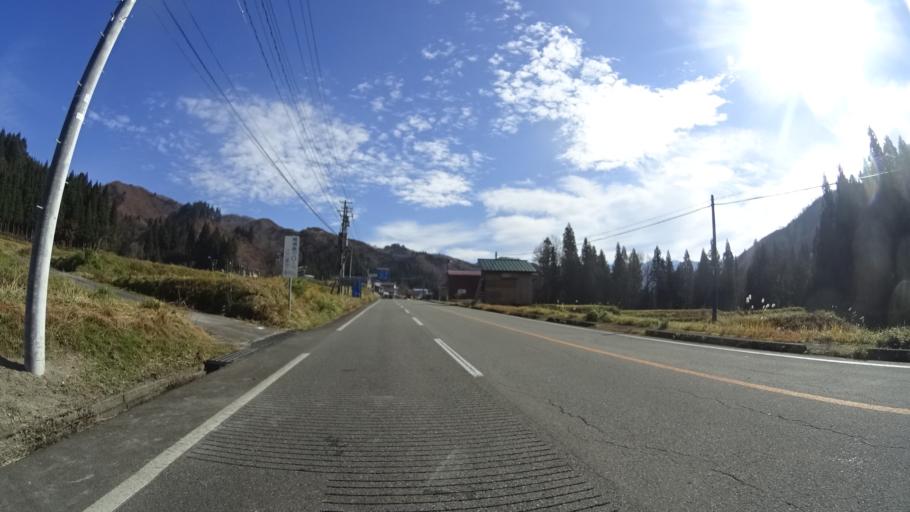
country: JP
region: Niigata
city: Muikamachi
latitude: 37.2054
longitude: 139.0695
